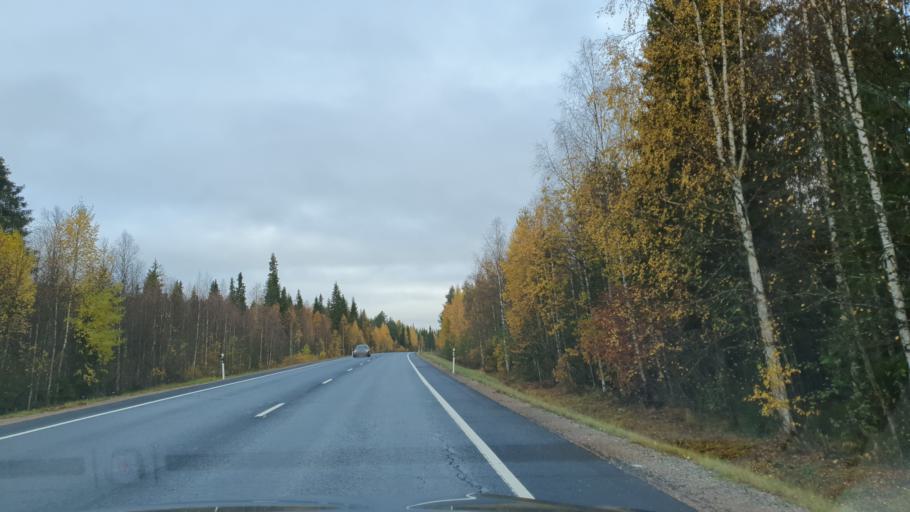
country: FI
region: Lapland
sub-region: Rovaniemi
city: Rovaniemi
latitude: 66.6135
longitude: 25.5559
